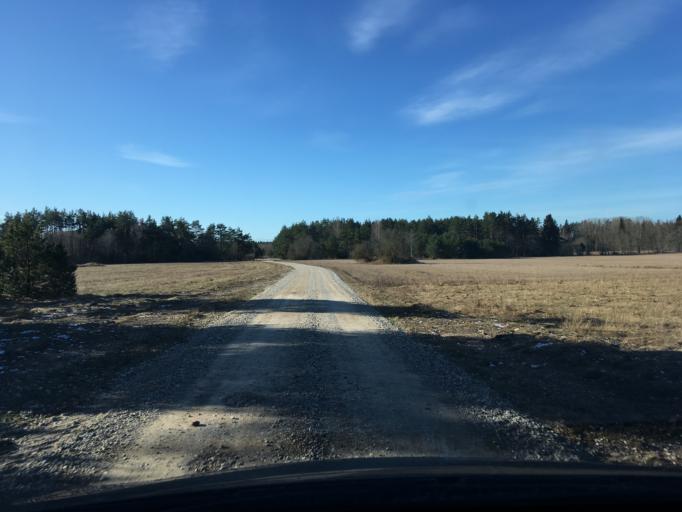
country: EE
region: Laeaene
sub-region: Lihula vald
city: Lihula
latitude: 58.5773
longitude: 23.7008
